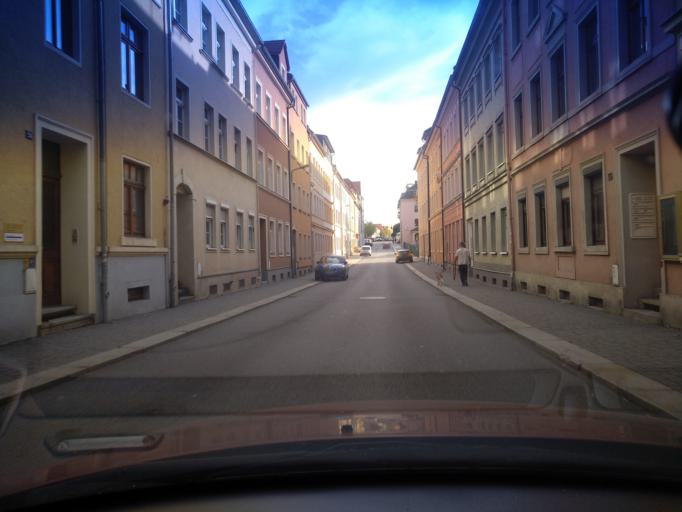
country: DE
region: Saxony
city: Bautzen
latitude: 51.1838
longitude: 14.4286
